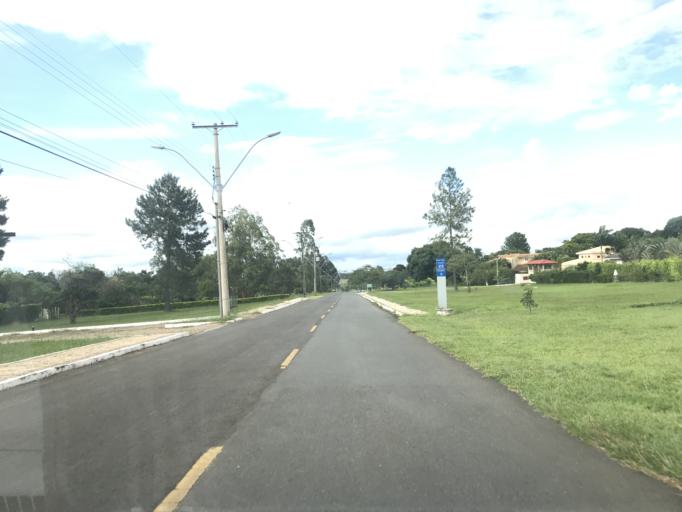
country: BR
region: Federal District
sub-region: Brasilia
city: Brasilia
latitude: -15.8941
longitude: -47.9190
